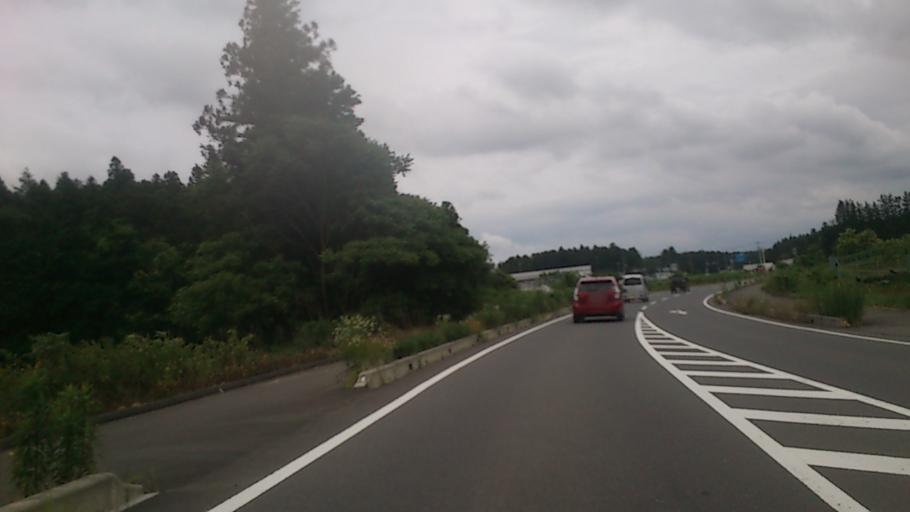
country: JP
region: Ibaraki
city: Ishioka
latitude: 36.2337
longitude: 140.3246
